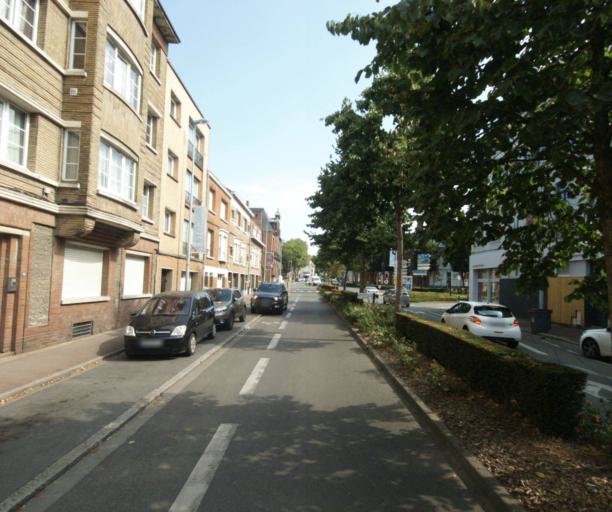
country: FR
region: Nord-Pas-de-Calais
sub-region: Departement du Nord
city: Tourcoing
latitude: 50.7159
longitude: 3.1579
